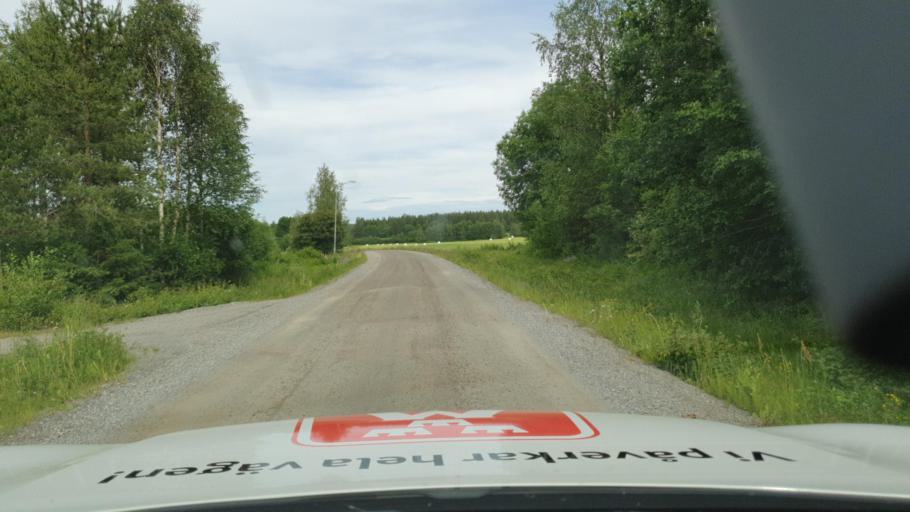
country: SE
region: Vaesterbotten
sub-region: Skelleftea Kommun
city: Viken
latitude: 64.5106
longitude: 20.9374
